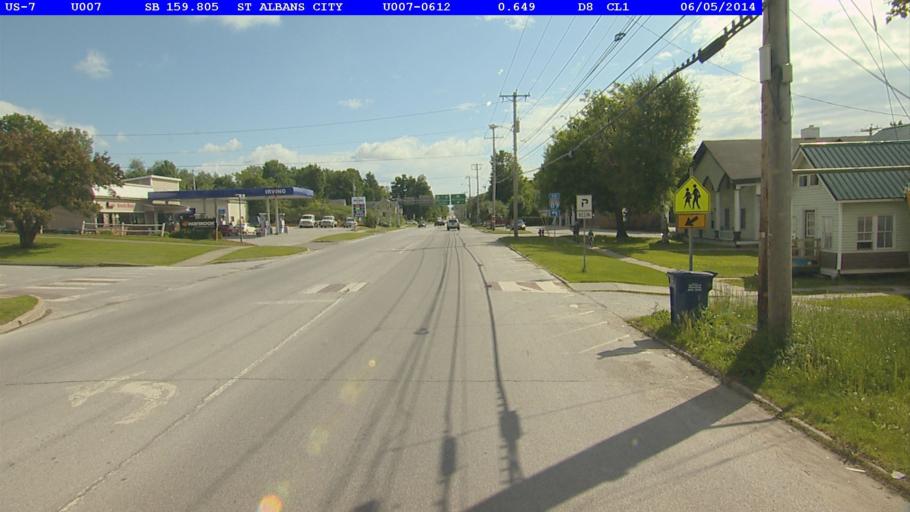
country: US
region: Vermont
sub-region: Franklin County
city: Saint Albans
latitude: 44.8029
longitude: -73.0878
